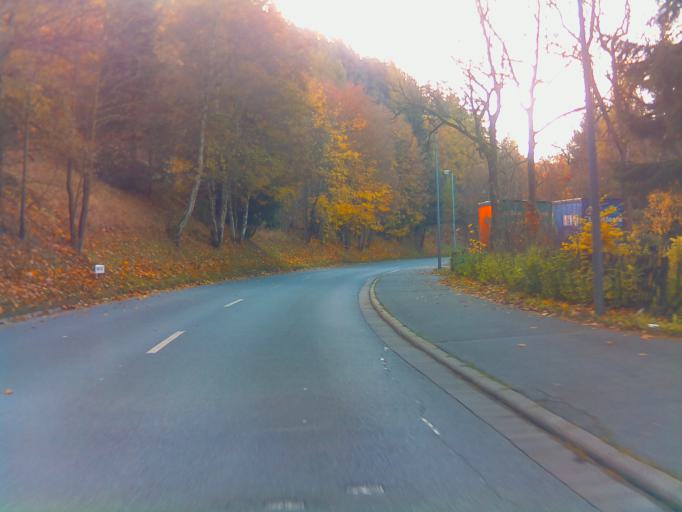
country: DE
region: Thuringia
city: Piesau
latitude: 50.5191
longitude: 11.2238
